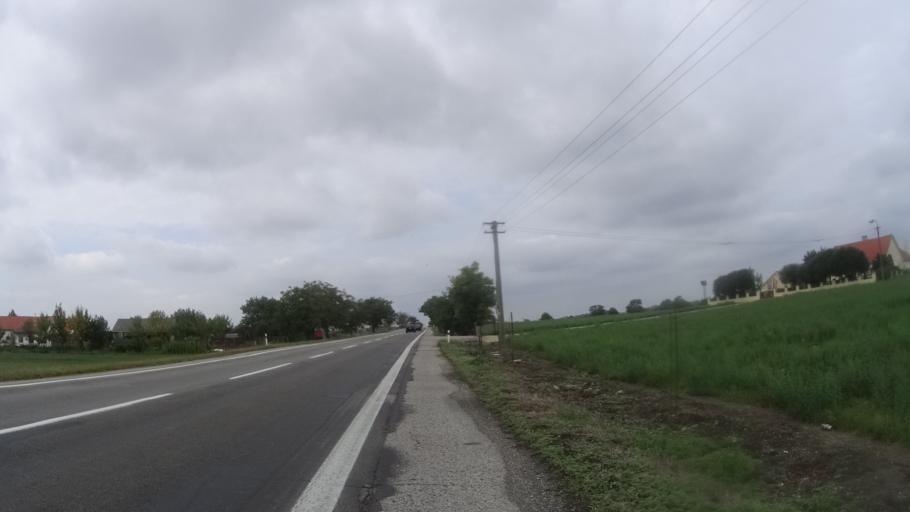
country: HU
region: Komarom-Esztergom
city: Acs
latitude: 47.7663
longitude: 18.0291
